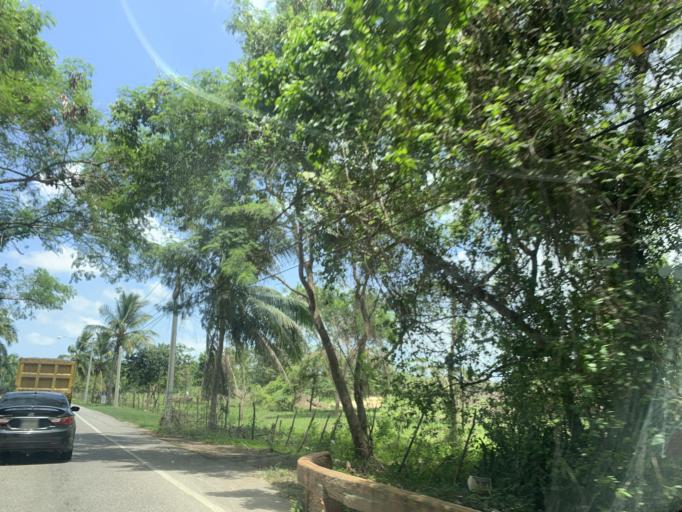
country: DO
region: Puerto Plata
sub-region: Puerto Plata
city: Puerto Plata
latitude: 19.7209
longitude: -70.6168
